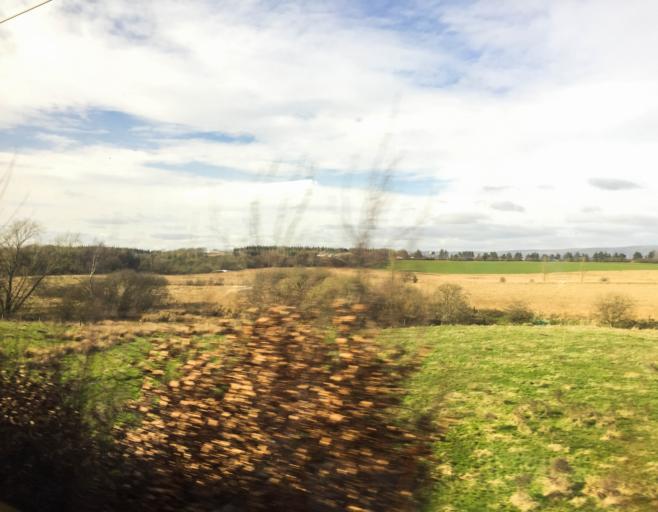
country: GB
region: Scotland
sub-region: North Lanarkshire
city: Stepps
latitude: 55.8895
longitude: -4.1560
